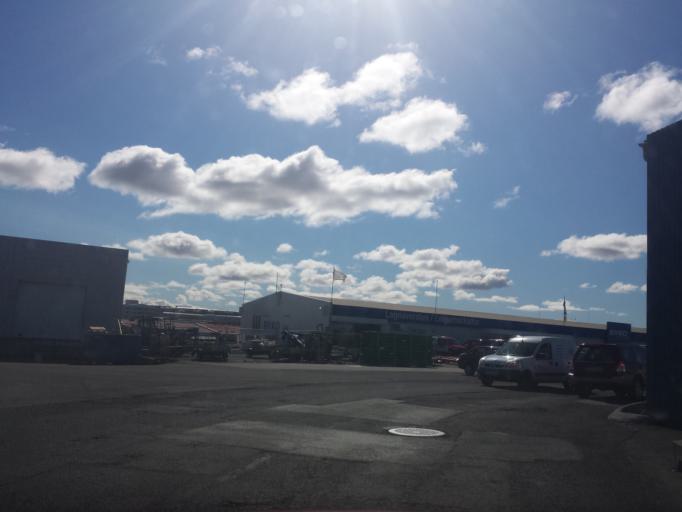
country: IS
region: Capital Region
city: Reykjavik
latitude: 64.1089
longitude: -21.8523
